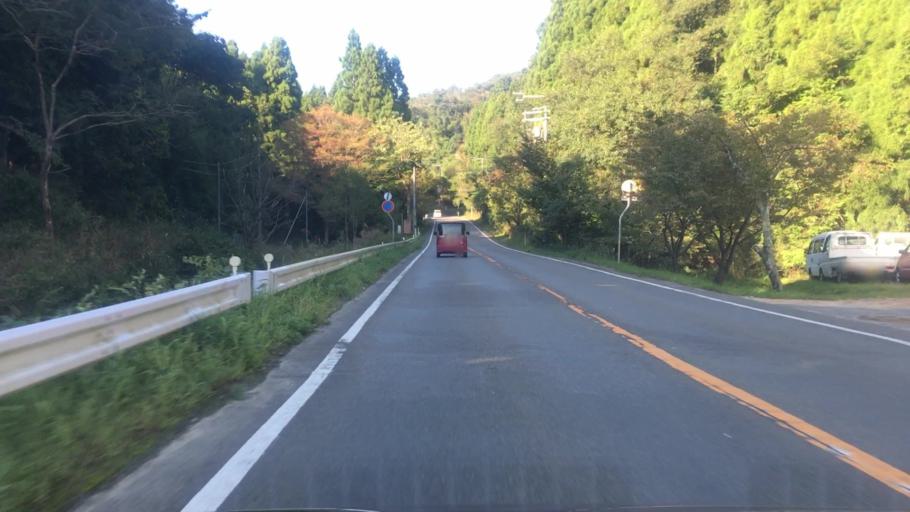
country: JP
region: Hyogo
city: Toyooka
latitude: 35.5641
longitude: 134.8524
